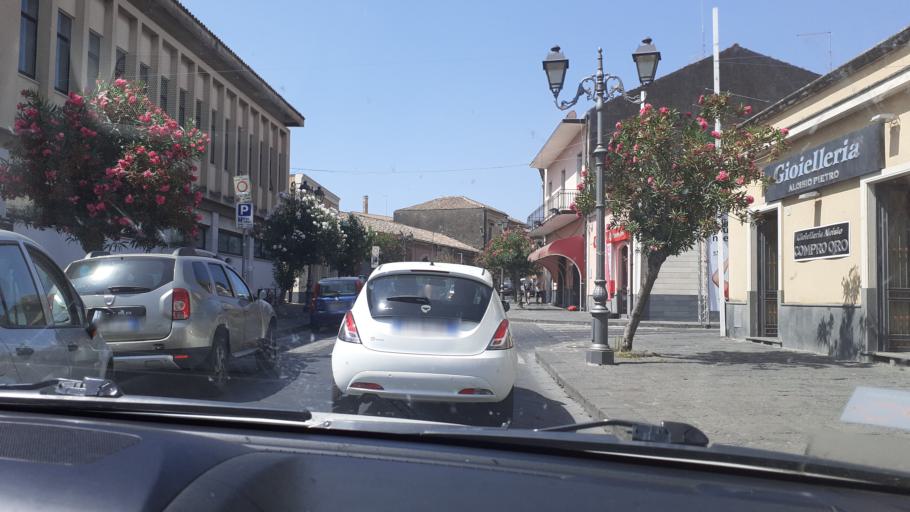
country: IT
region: Sicily
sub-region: Catania
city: Pedara
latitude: 37.6174
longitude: 15.0600
